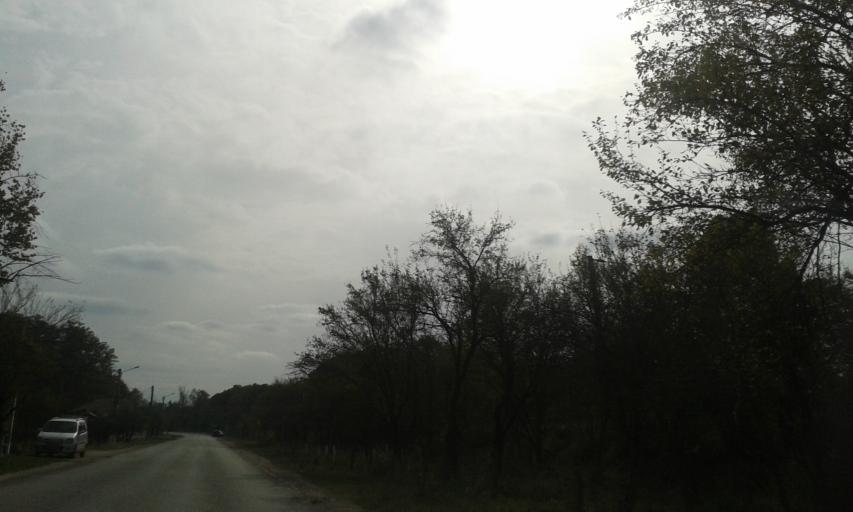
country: RO
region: Gorj
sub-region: Comuna Targu Carbunesti
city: Targu Carbunesti
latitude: 44.9700
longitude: 23.5030
